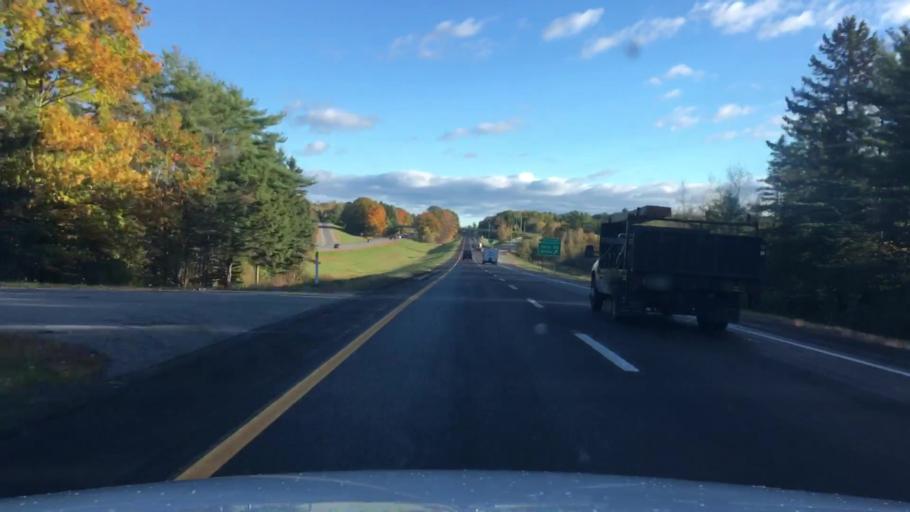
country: US
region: Maine
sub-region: Penobscot County
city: Veazie
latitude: 44.8677
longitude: -68.7066
